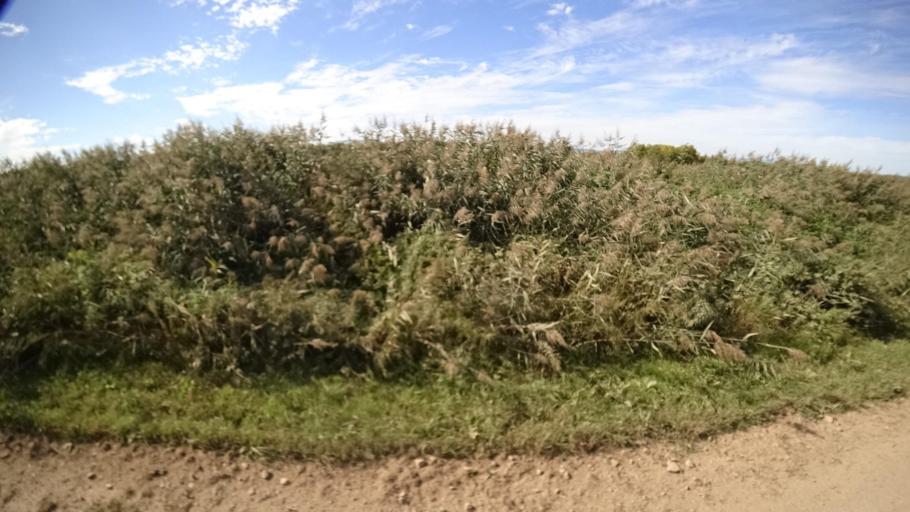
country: RU
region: Primorskiy
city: Yakovlevka
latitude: 44.4240
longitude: 133.5738
